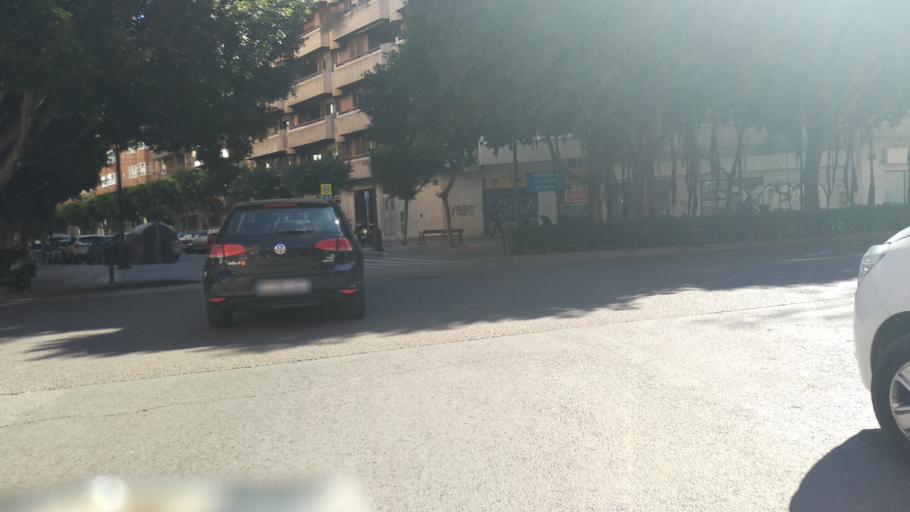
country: ES
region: Valencia
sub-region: Provincia de Valencia
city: Valencia
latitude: 39.4633
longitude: -0.3857
